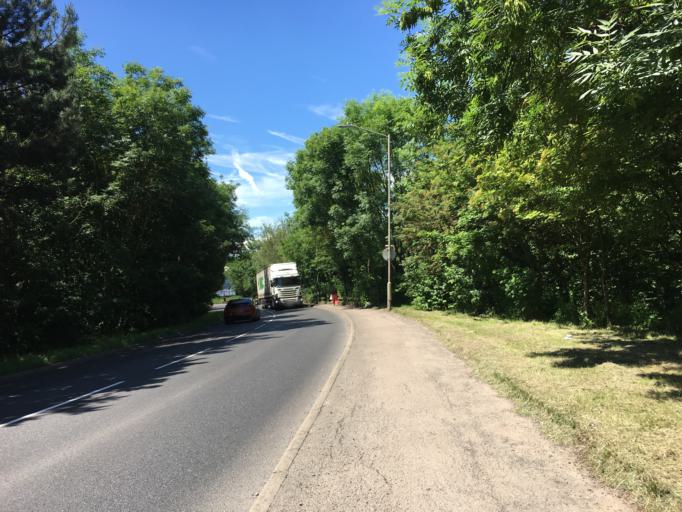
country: GB
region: England
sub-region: Warwickshire
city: Rugby
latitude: 52.3928
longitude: -1.2585
